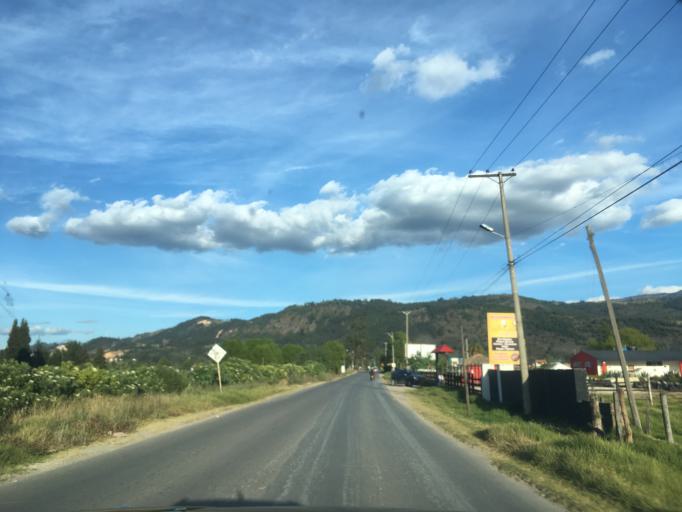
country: CO
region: Boyaca
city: Firavitoba
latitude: 5.6650
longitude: -72.9699
